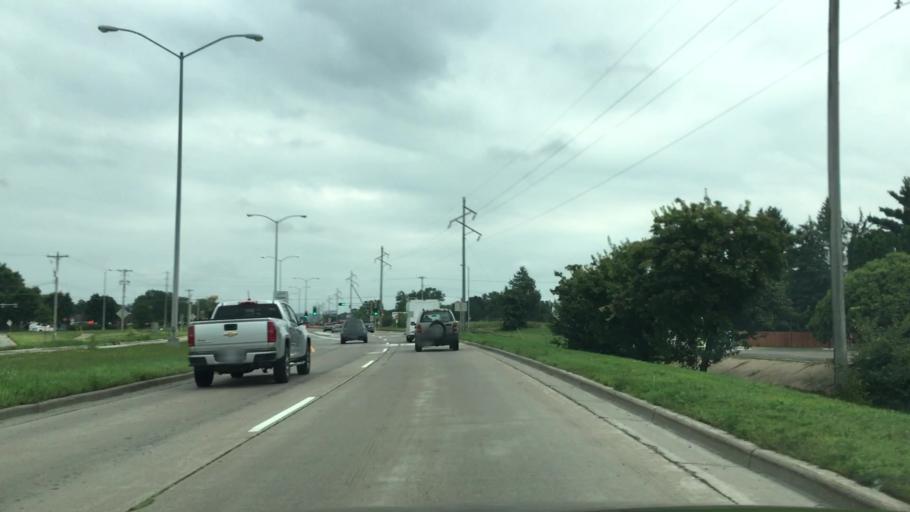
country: US
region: Wisconsin
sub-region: Eau Claire County
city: Eau Claire
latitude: 44.8209
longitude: -91.5439
